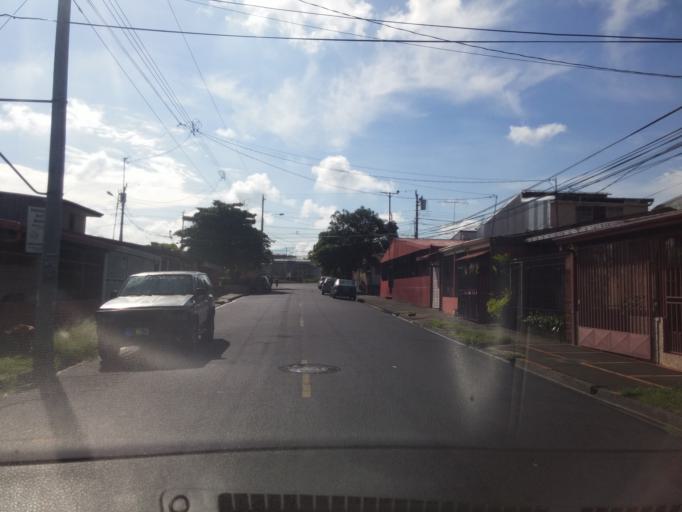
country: CR
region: Heredia
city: San Francisco
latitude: 9.9976
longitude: -84.1270
